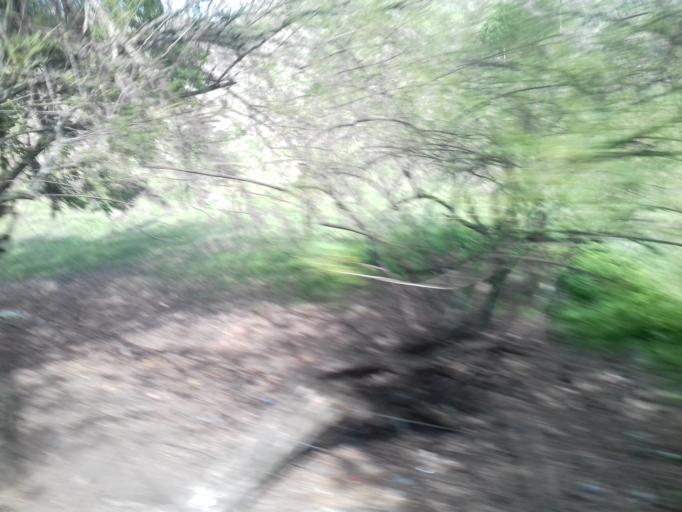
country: CO
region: Antioquia
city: Tarso
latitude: 5.9648
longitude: -75.8445
